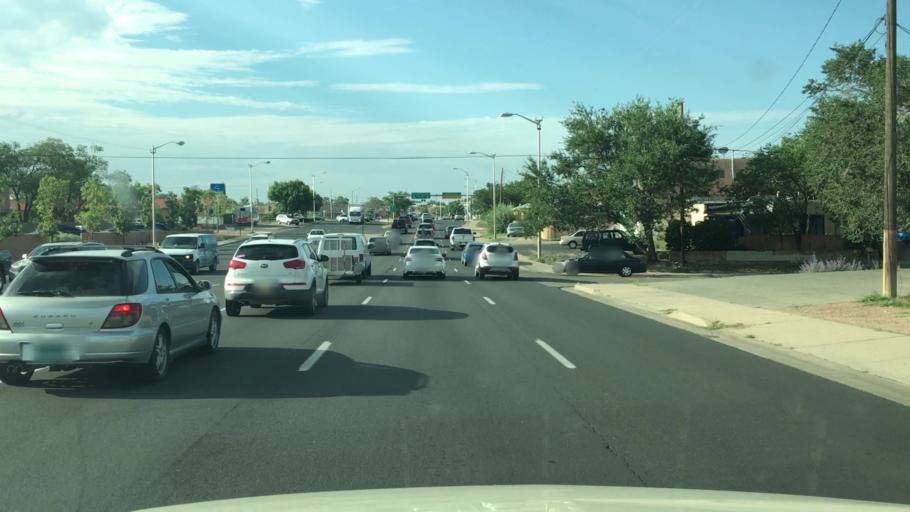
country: US
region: New Mexico
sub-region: Santa Fe County
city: Santa Fe
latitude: 35.6803
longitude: -105.9545
